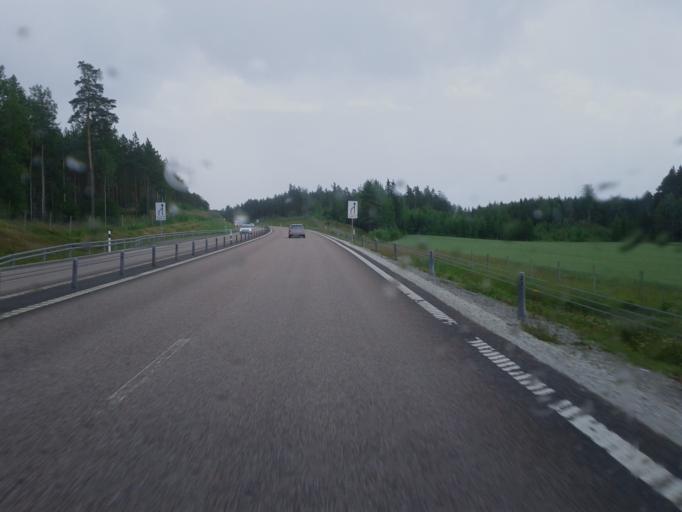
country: SE
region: Vaestmanland
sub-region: Sala Kommun
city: Sala
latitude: 59.9017
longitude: 16.5374
